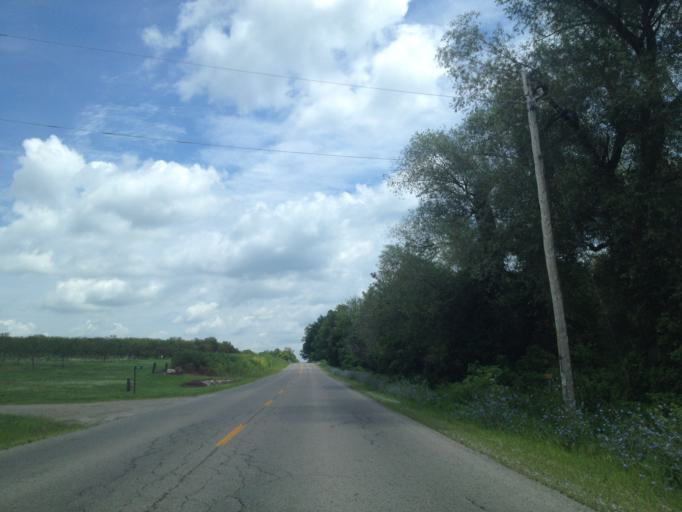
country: CA
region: Ontario
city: Norfolk County
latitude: 42.7747
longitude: -80.2730
